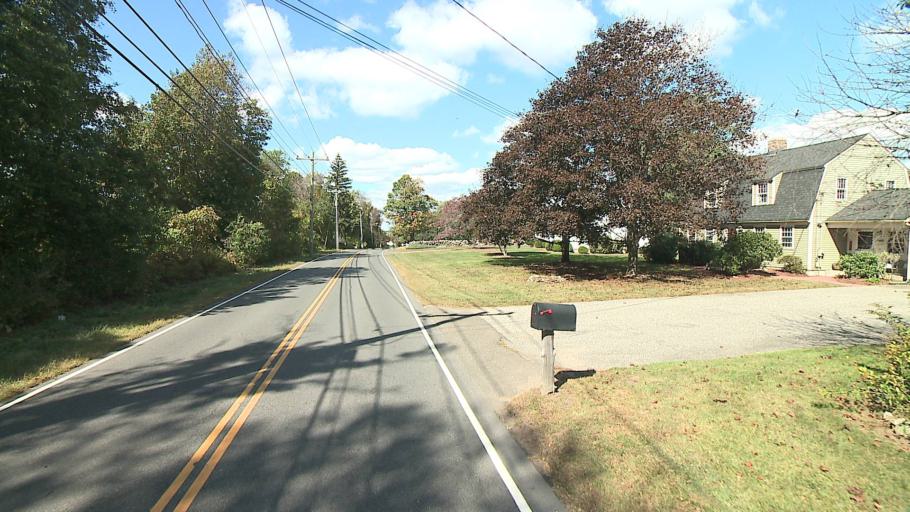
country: US
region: Connecticut
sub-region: New Haven County
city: Ansonia
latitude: 41.3634
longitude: -73.1166
